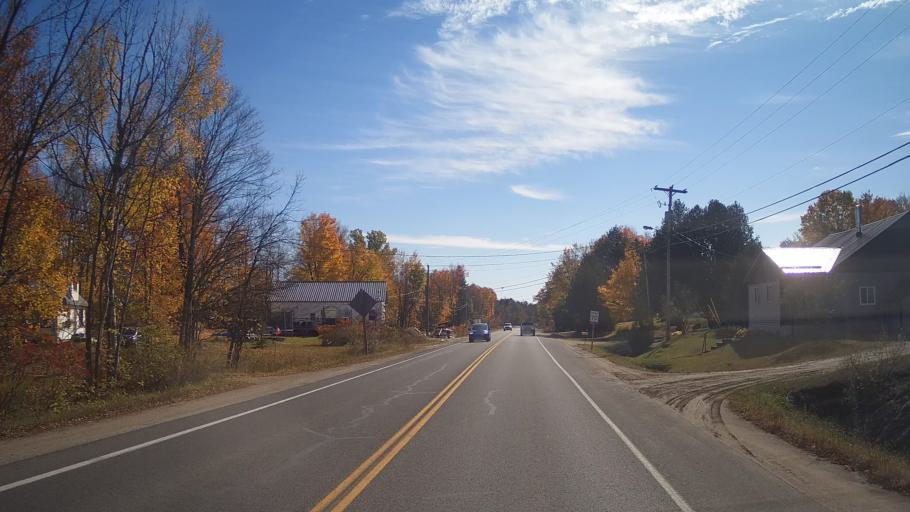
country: CA
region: Ontario
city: Perth
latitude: 44.7969
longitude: -76.6787
